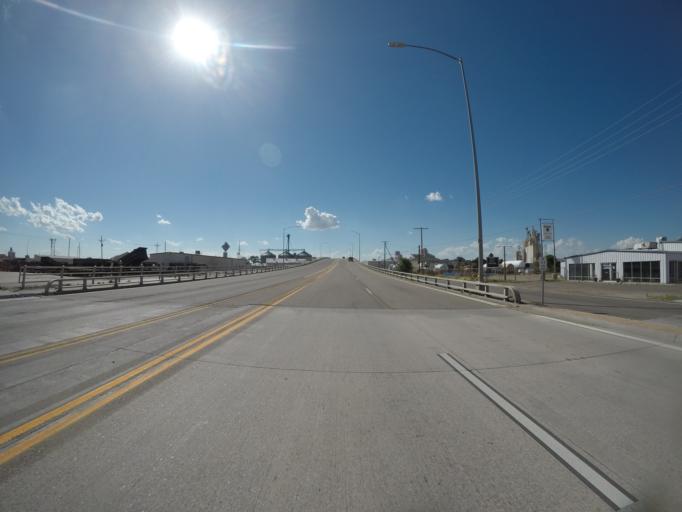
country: US
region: Colorado
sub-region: Logan County
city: Sterling
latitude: 40.6234
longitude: -103.1999
